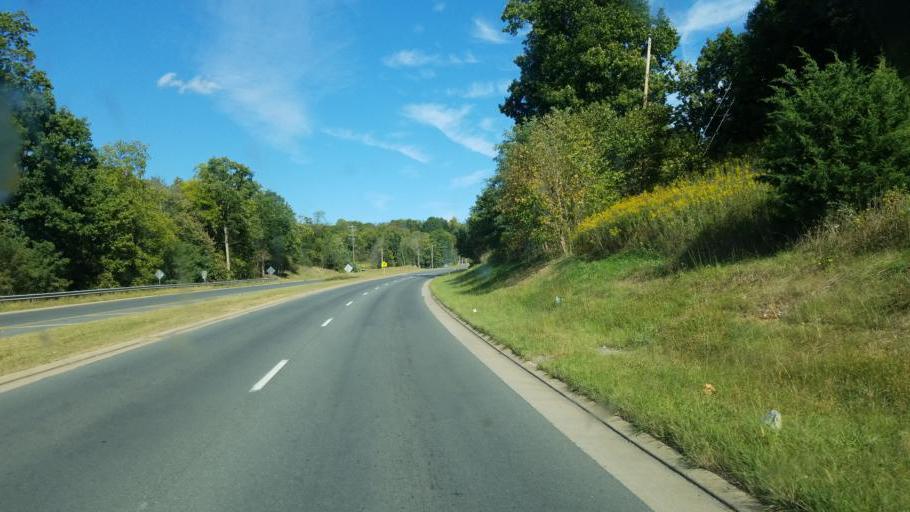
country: US
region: Virginia
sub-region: Warren County
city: Front Royal
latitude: 38.9035
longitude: -78.2102
